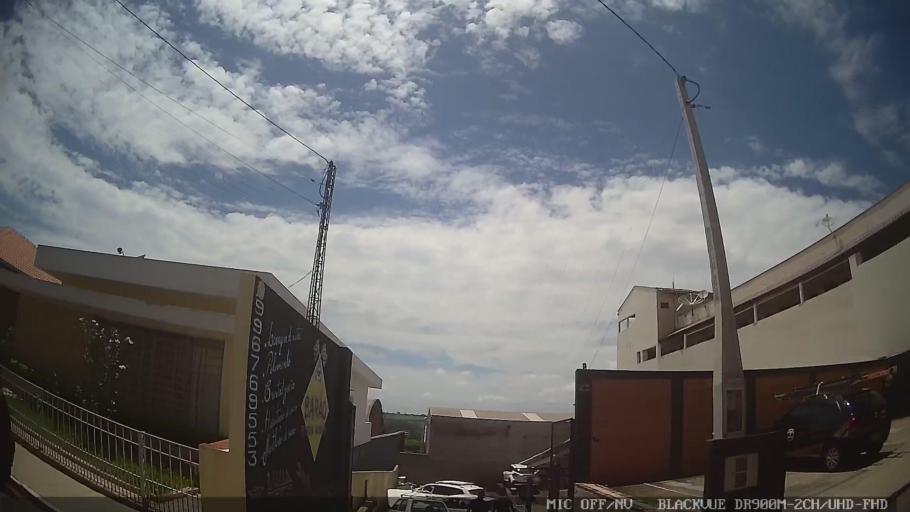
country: BR
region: Sao Paulo
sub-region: Laranjal Paulista
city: Laranjal Paulista
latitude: -23.0458
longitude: -47.8352
